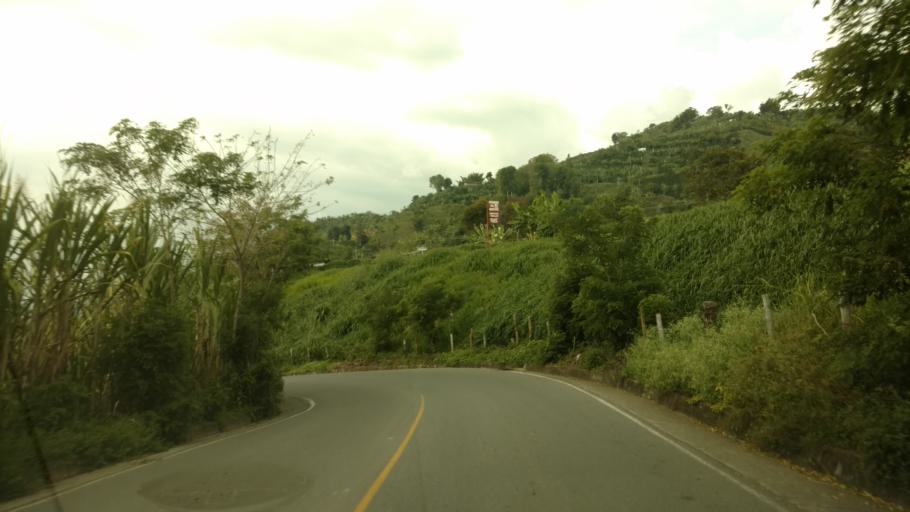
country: CO
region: Caldas
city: Neira
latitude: 5.1853
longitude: -75.5496
